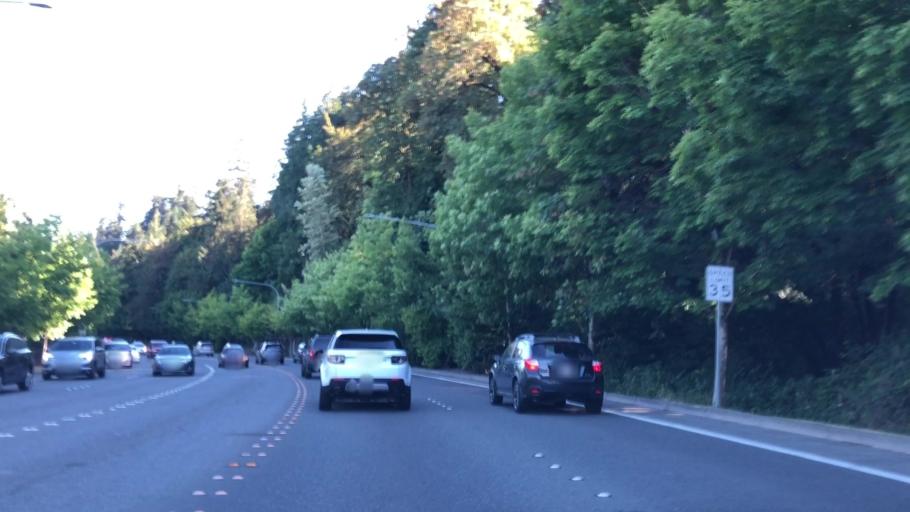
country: US
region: Washington
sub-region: King County
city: Redmond
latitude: 47.6648
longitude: -122.1273
